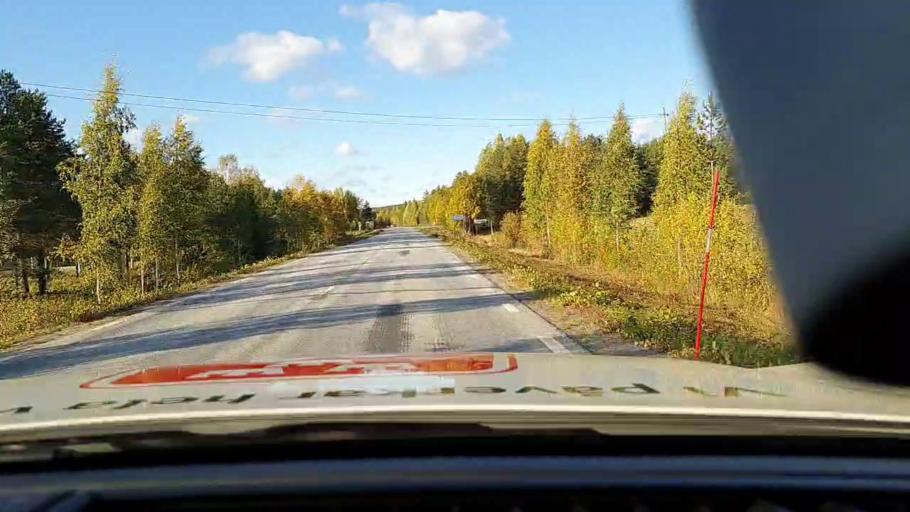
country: SE
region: Norrbotten
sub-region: Pitea Kommun
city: Norrfjarden
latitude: 65.4588
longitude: 21.4541
